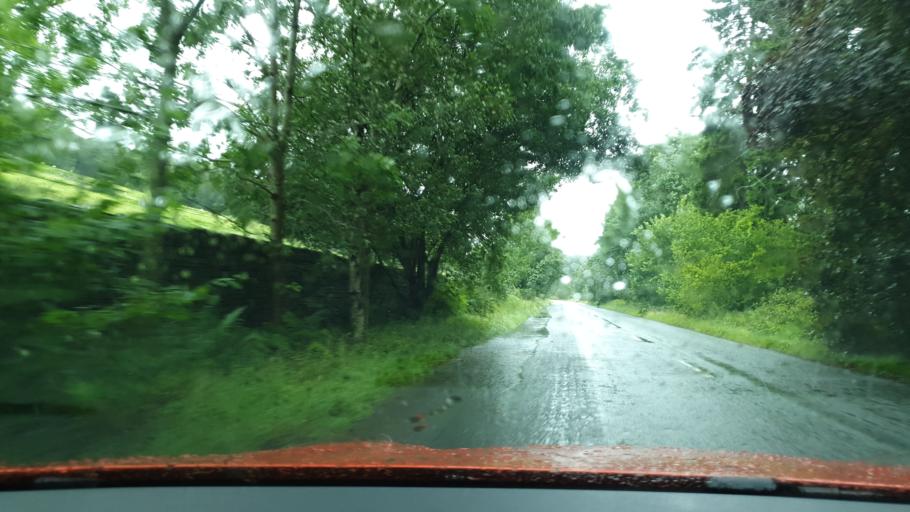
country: GB
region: England
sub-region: Cumbria
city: Ulverston
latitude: 54.3191
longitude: -3.0919
